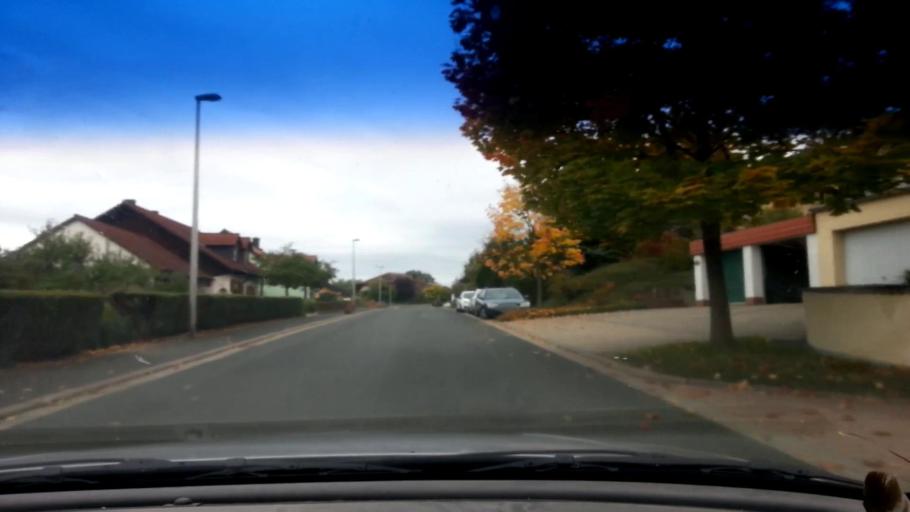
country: DE
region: Bavaria
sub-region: Upper Franconia
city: Priesendorf
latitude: 49.9088
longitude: 10.7077
